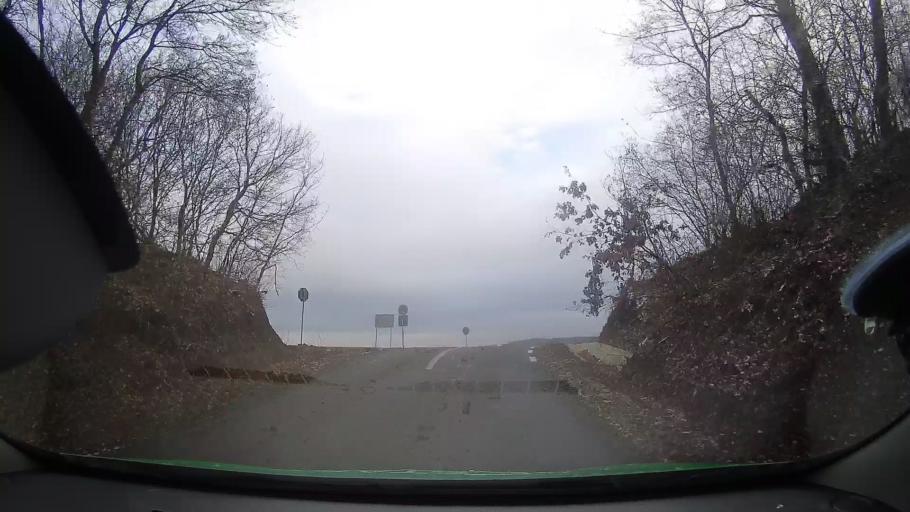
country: RO
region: Mures
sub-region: Comuna Ludus
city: Gheja
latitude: 46.3995
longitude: 24.0202
